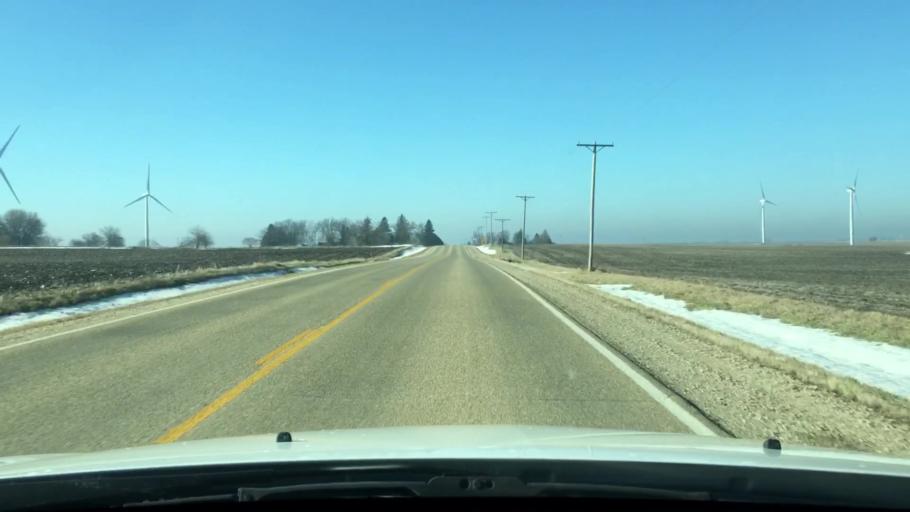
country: US
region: Illinois
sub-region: DeKalb County
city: Malta
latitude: 41.8486
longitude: -88.9191
